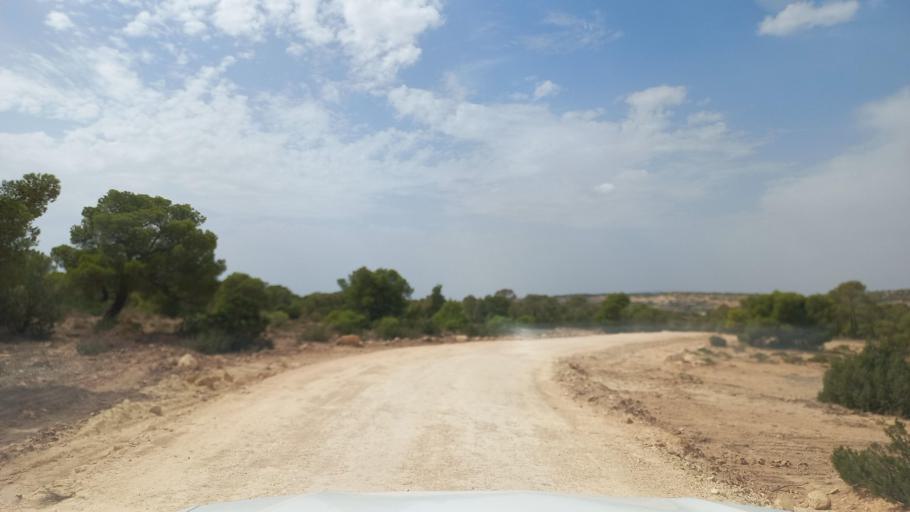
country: TN
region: Al Qasrayn
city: Kasserine
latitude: 35.3823
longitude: 8.8764
